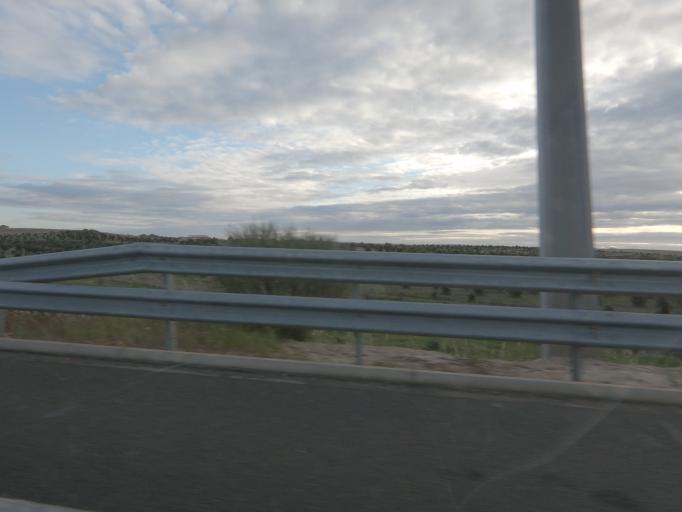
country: ES
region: Extremadura
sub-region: Provincia de Caceres
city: Caceres
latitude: 39.4720
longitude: -6.4265
